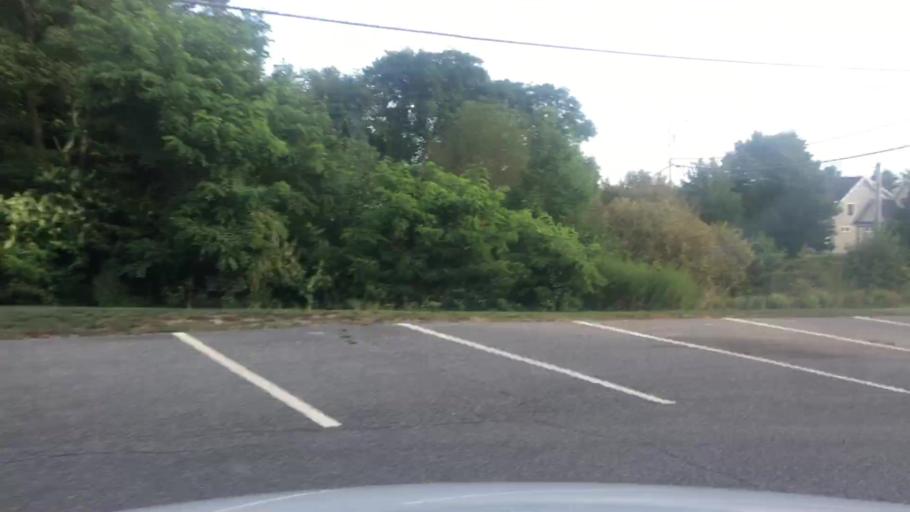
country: US
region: Maine
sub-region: Cumberland County
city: Scarborough
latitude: 43.5963
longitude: -70.3231
